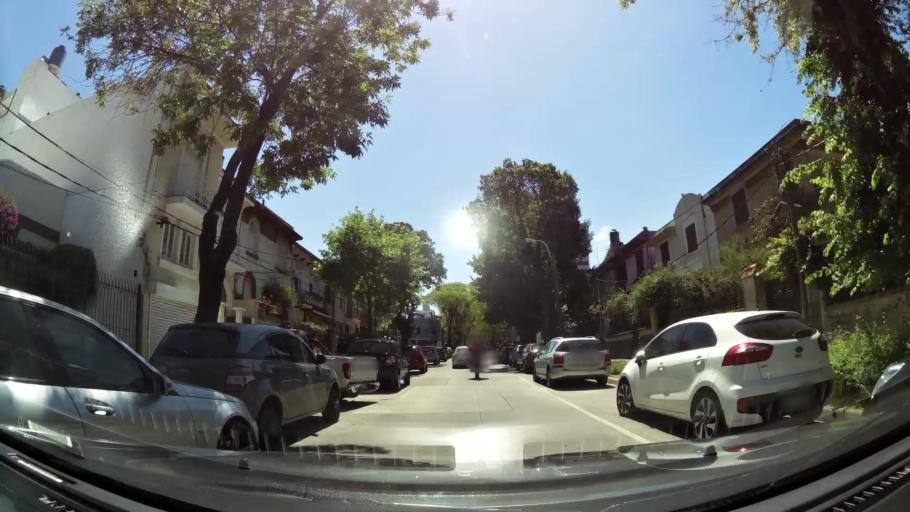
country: UY
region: Montevideo
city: Montevideo
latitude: -34.9225
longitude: -56.1577
